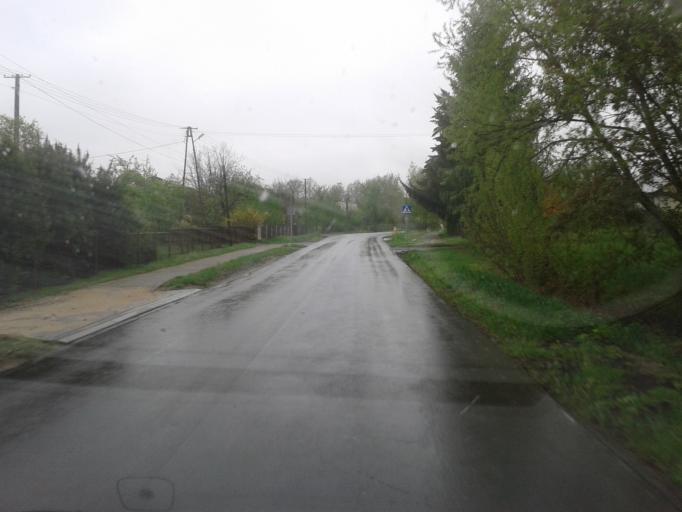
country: PL
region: Lublin Voivodeship
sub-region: Powiat tomaszowski
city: Lubycza Krolewska
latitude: 50.3439
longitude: 23.5201
